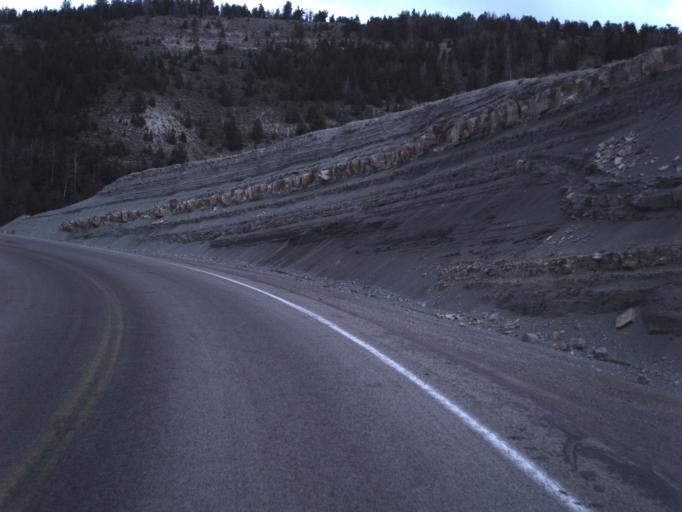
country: US
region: Utah
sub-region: Carbon County
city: Helper
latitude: 39.8667
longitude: -110.7639
